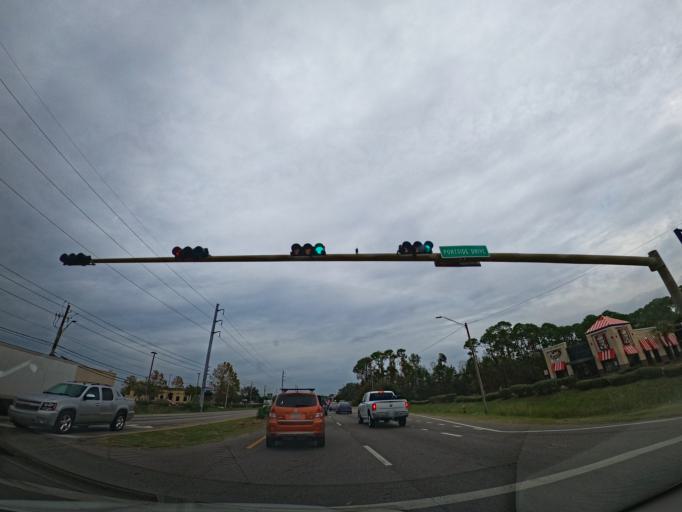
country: US
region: Florida
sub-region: Santa Rosa County
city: Tiger Point
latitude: 30.3899
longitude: -87.0617
